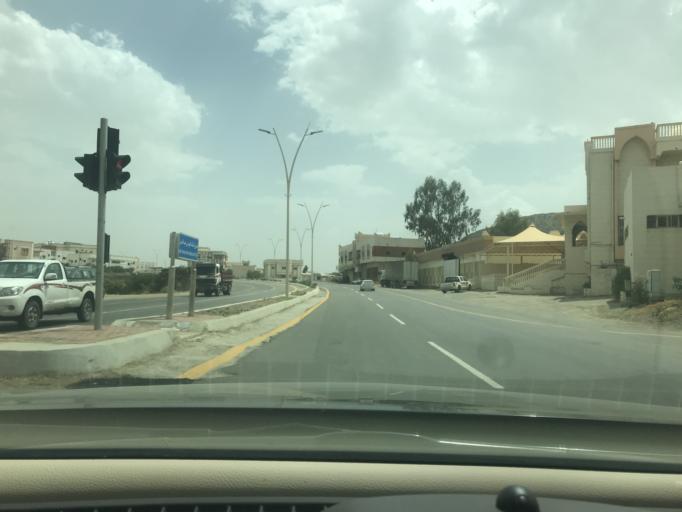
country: SA
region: Mintaqat al Bahah
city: Al Bahah
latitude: 20.0503
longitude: 41.4993
